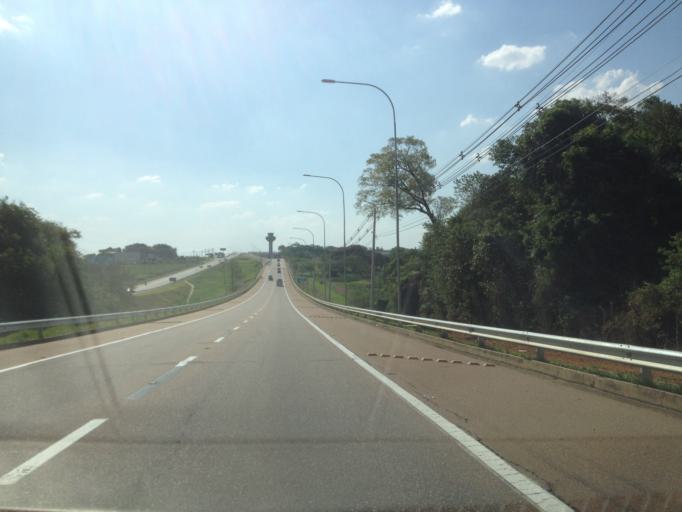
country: BR
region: Sao Paulo
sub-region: Indaiatuba
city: Indaiatuba
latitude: -23.0185
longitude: -47.1345
